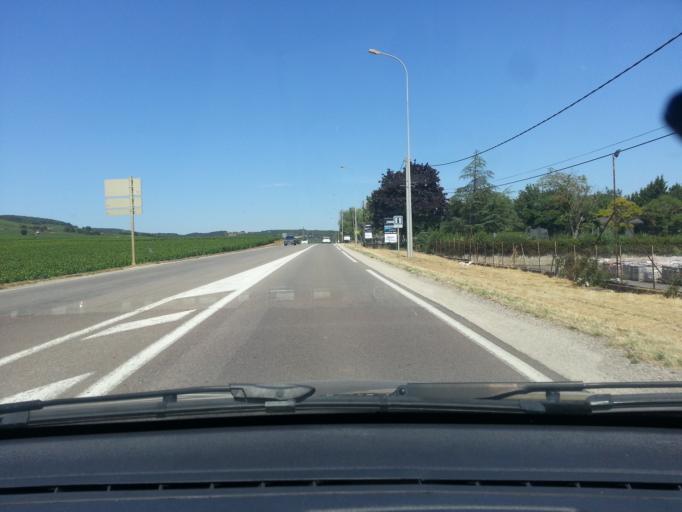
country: FR
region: Bourgogne
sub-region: Departement de la Cote-d'Or
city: Beaune
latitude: 47.0656
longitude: 4.8688
